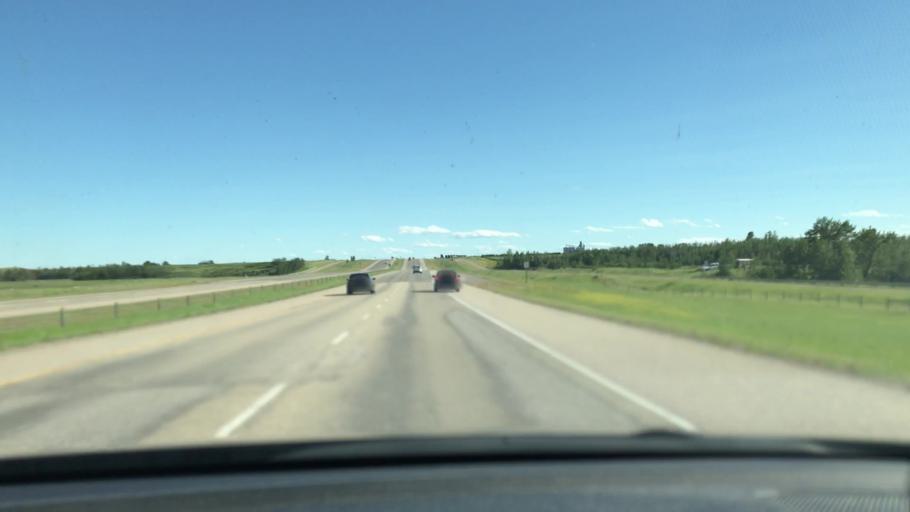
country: CA
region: Alberta
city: Crossfield
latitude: 51.5198
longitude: -114.0253
